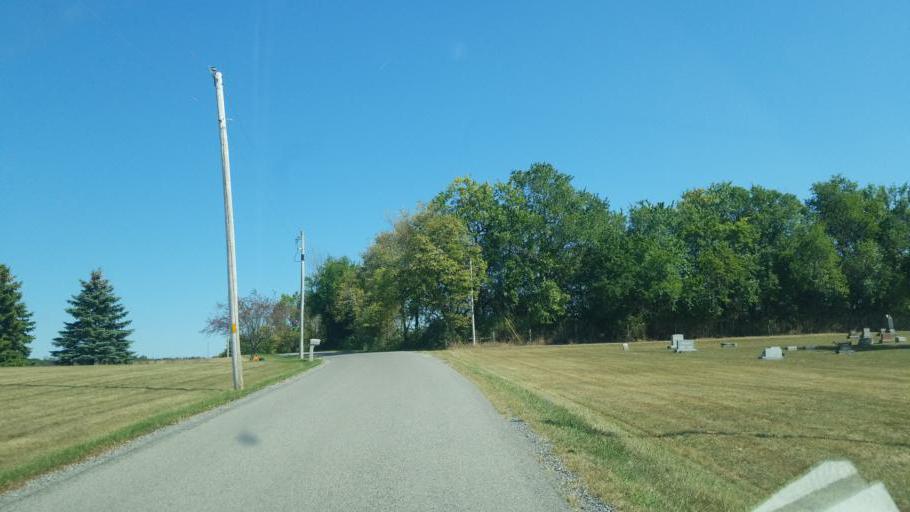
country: US
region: Ohio
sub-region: Logan County
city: Bellefontaine
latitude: 40.4232
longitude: -83.7835
